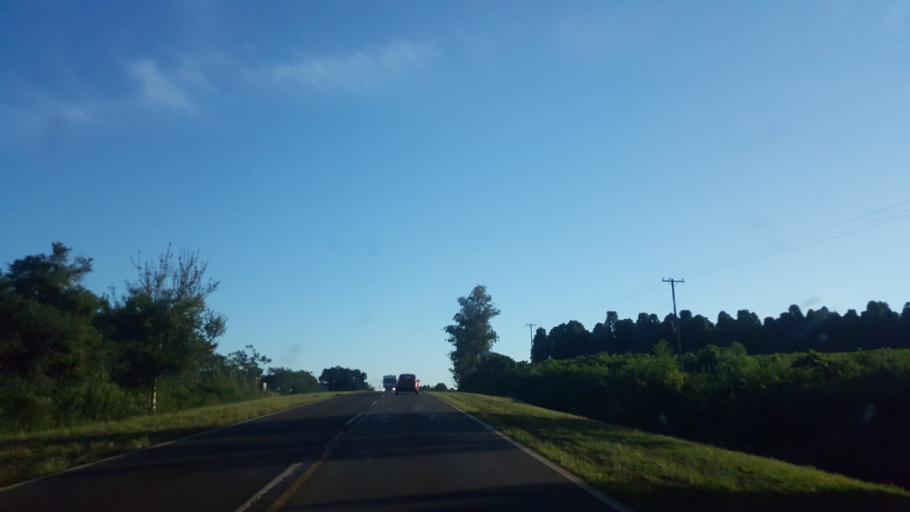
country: AR
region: Misiones
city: El Alcazar
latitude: -26.7421
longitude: -54.8797
